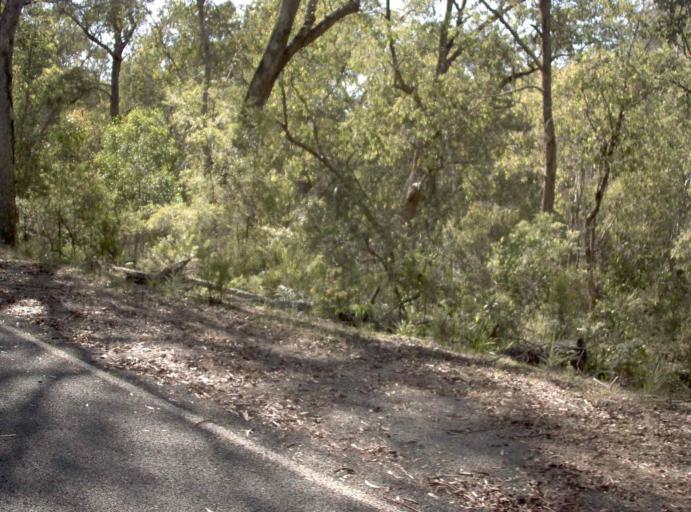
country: AU
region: New South Wales
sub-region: Bombala
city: Bombala
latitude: -37.3787
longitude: 148.6627
